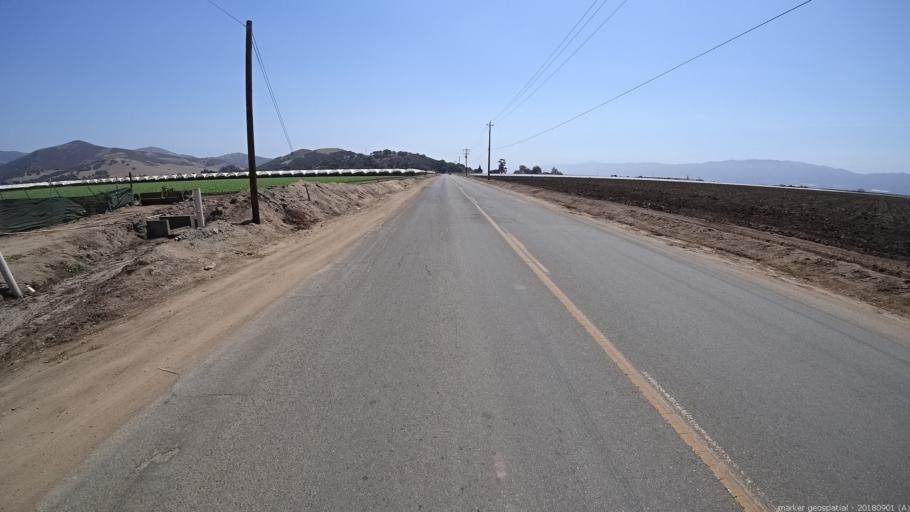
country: US
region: California
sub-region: Monterey County
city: Salinas
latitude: 36.6983
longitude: -121.5739
